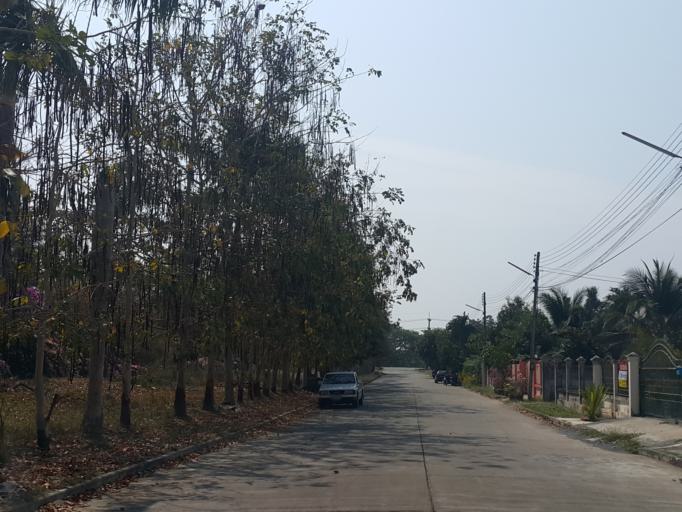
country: TH
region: Chiang Mai
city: San Kamphaeng
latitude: 18.7387
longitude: 99.1141
